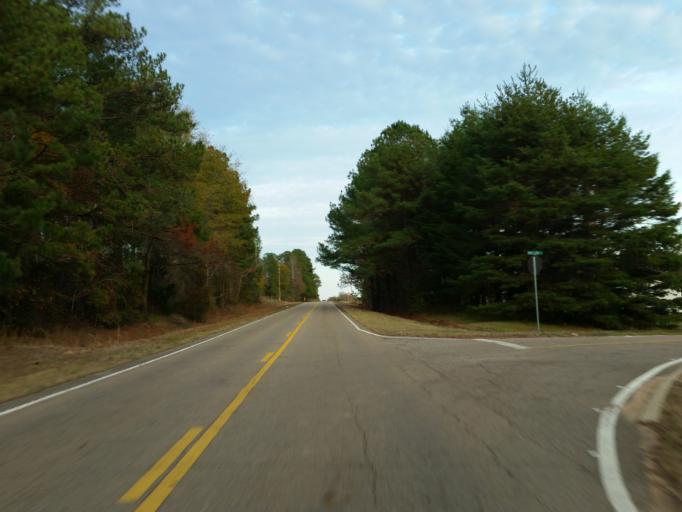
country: US
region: Mississippi
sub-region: Lauderdale County
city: Marion
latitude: 32.4234
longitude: -88.4764
